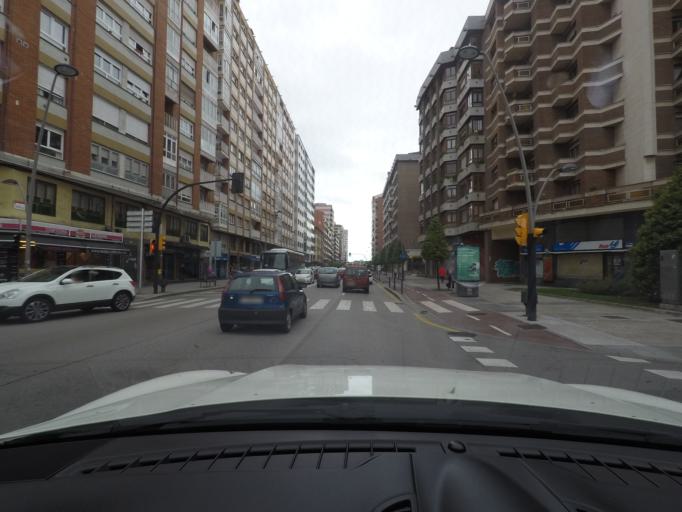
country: ES
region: Asturias
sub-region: Province of Asturias
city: Gijon
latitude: 43.5361
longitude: -5.6478
